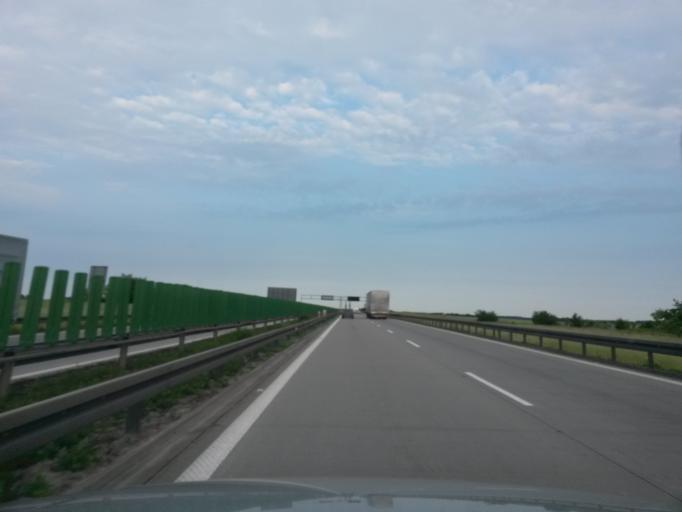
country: PL
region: Lower Silesian Voivodeship
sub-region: Powiat sredzki
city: Ciechow
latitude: 51.0364
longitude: 16.6181
